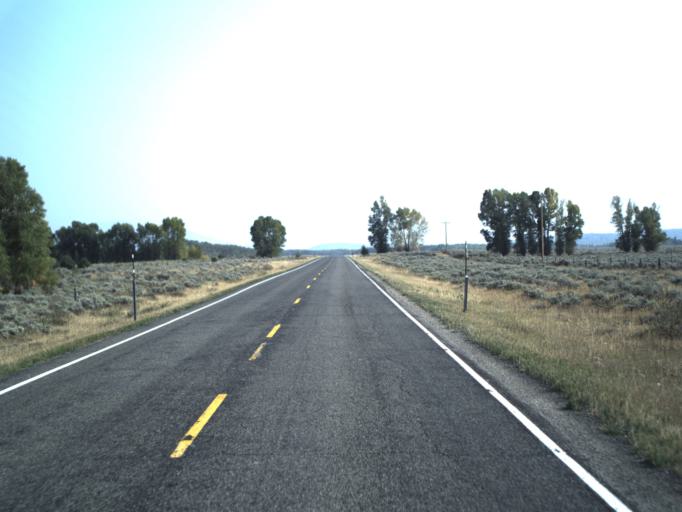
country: US
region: Wyoming
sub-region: Uinta County
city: Evanston
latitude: 40.9771
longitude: -110.8532
